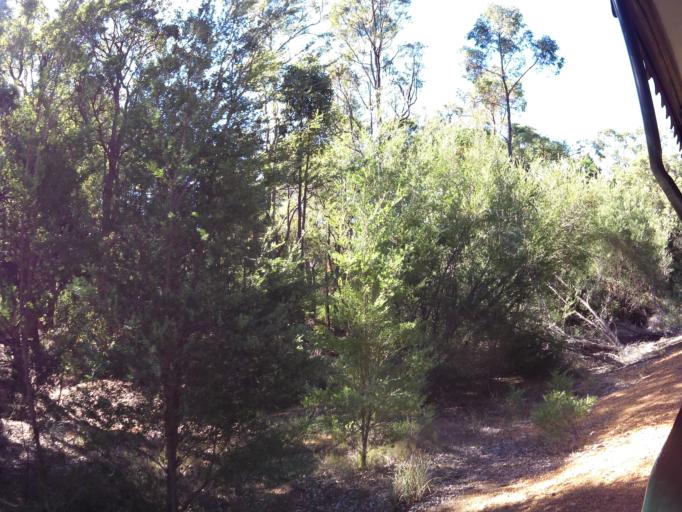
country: AU
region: Western Australia
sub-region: Waroona
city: Waroona
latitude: -32.7090
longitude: 116.0672
